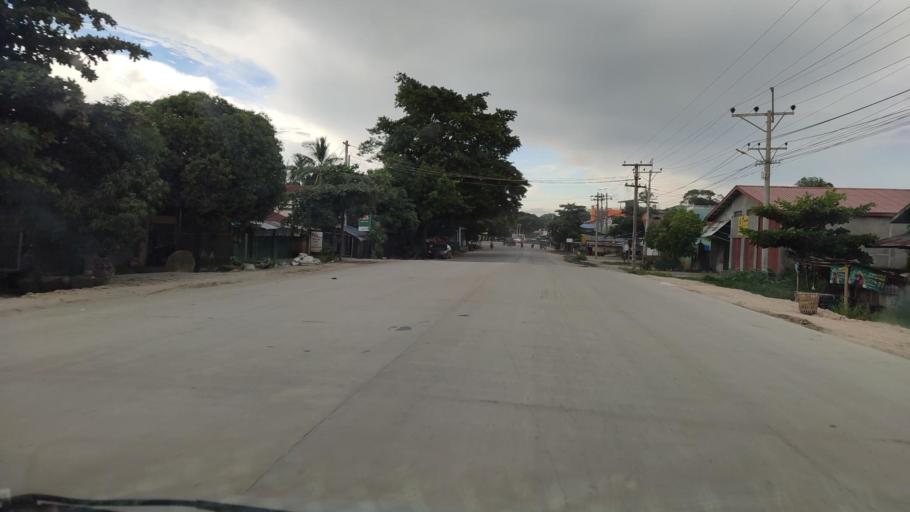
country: MM
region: Bago
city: Taungoo
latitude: 18.9071
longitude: 96.4441
